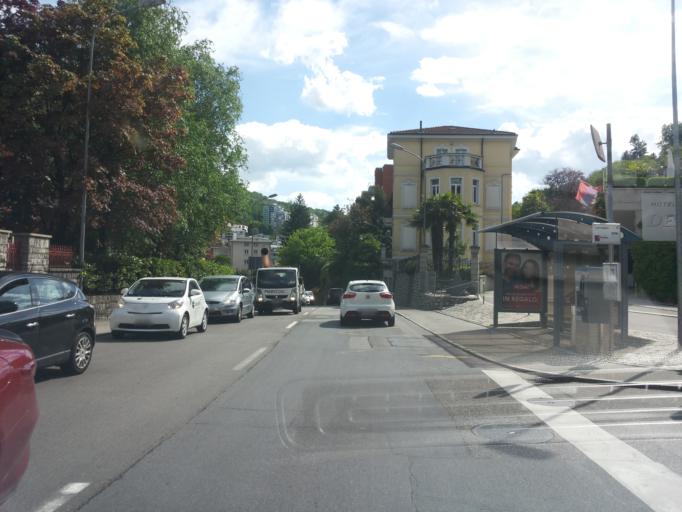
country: CH
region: Ticino
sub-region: Lugano District
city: Sorengo
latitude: 45.9939
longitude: 8.9429
